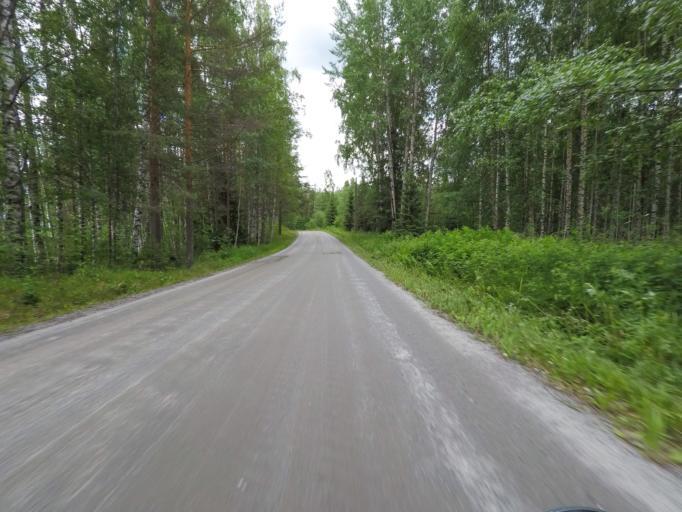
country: FI
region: Central Finland
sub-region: Jyvaeskylae
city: Hankasalmi
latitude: 62.4259
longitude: 26.6450
